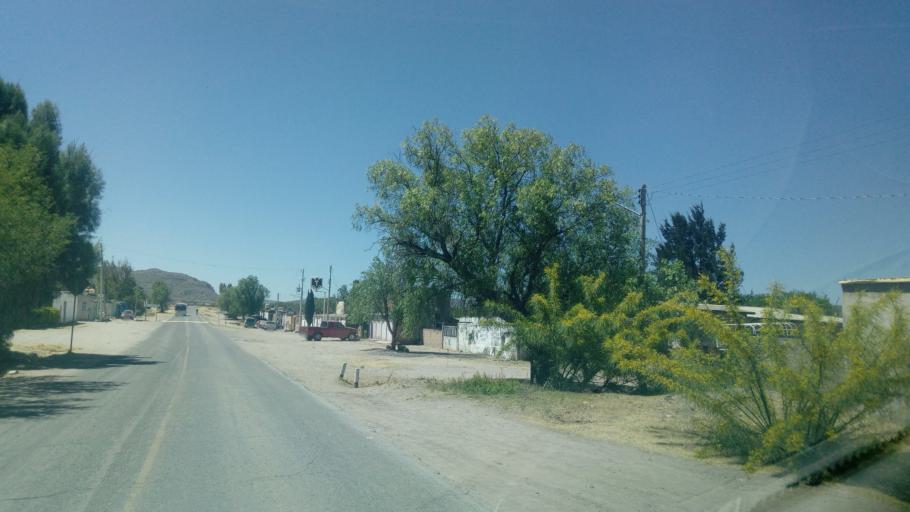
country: MX
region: Durango
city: Victoria de Durango
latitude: 24.1687
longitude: -104.7032
